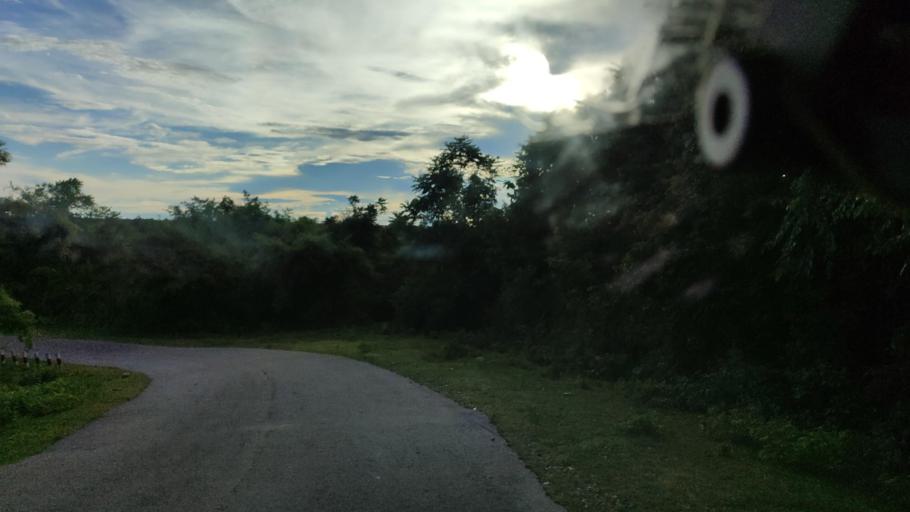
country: MM
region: Mandalay
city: Nay Pyi Taw
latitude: 19.9977
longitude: 95.9169
